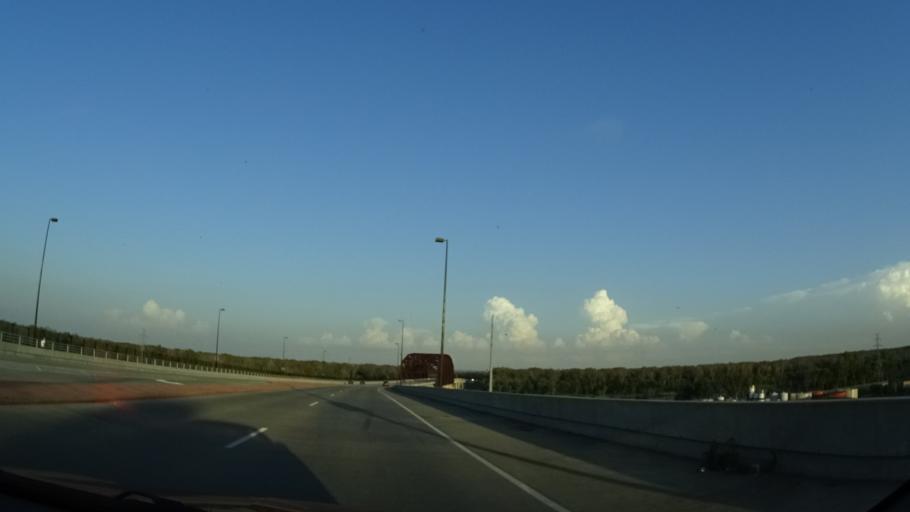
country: US
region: Nebraska
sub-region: Douglas County
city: Omaha
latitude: 41.2128
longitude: -95.9323
